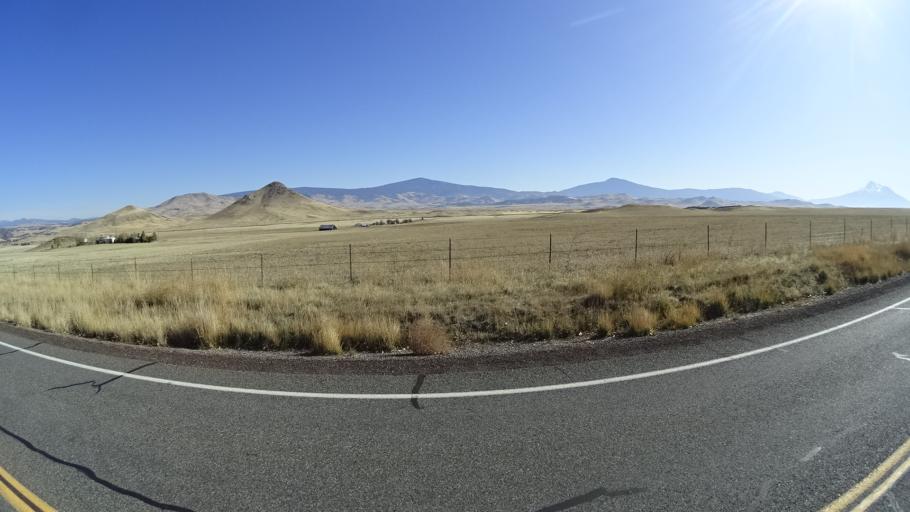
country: US
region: California
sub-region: Siskiyou County
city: Montague
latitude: 41.8132
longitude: -122.4983
